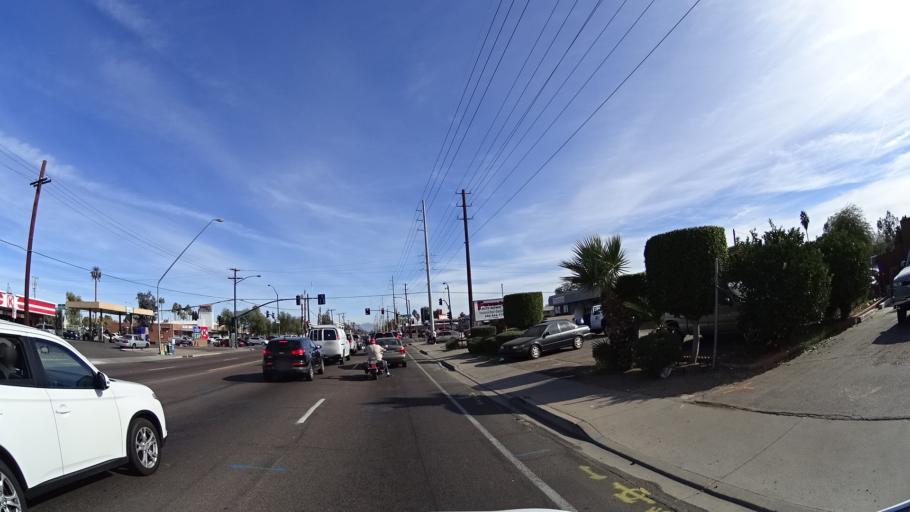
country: US
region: Arizona
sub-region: Maricopa County
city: Mesa
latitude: 33.4077
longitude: -111.8239
